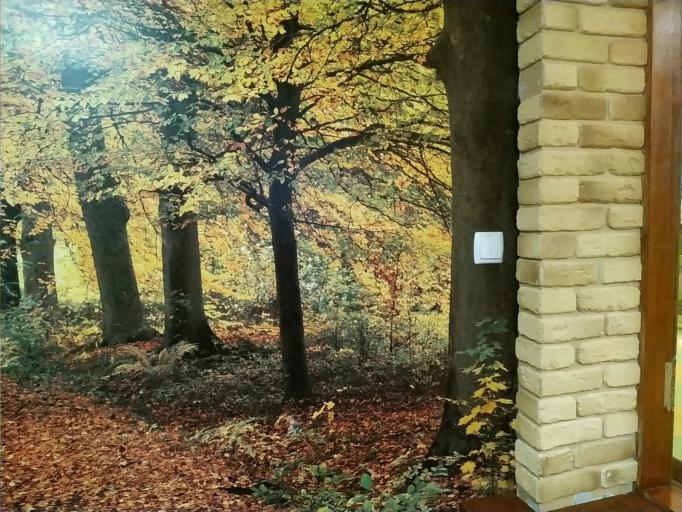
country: RU
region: Smolensk
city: Safonovo
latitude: 55.2028
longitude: 33.2402
